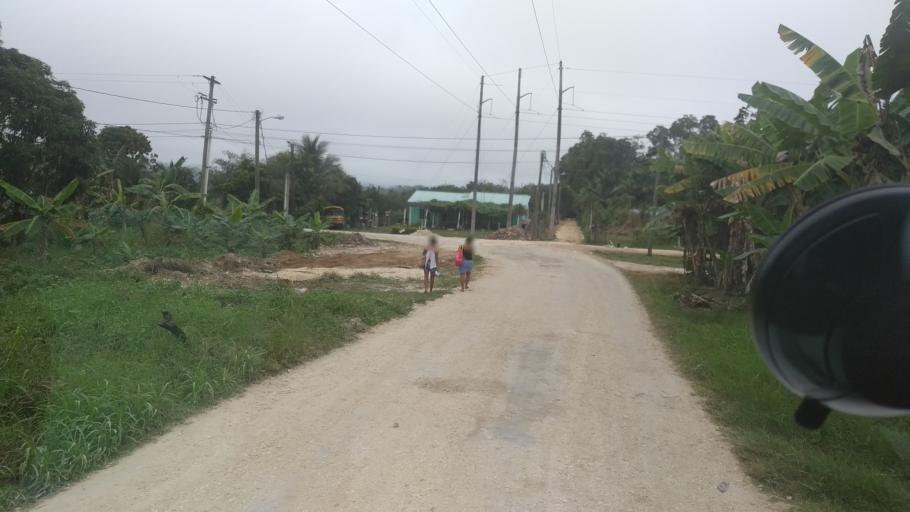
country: BZ
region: Cayo
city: Benque Viejo del Carmen
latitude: 17.0828
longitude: -89.1245
